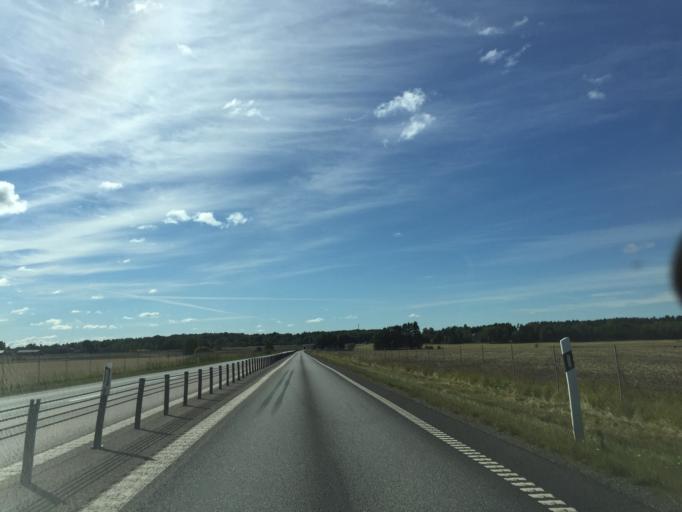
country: SE
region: Vaestmanland
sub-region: Kopings Kommun
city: Koping
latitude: 59.5587
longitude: 16.0561
